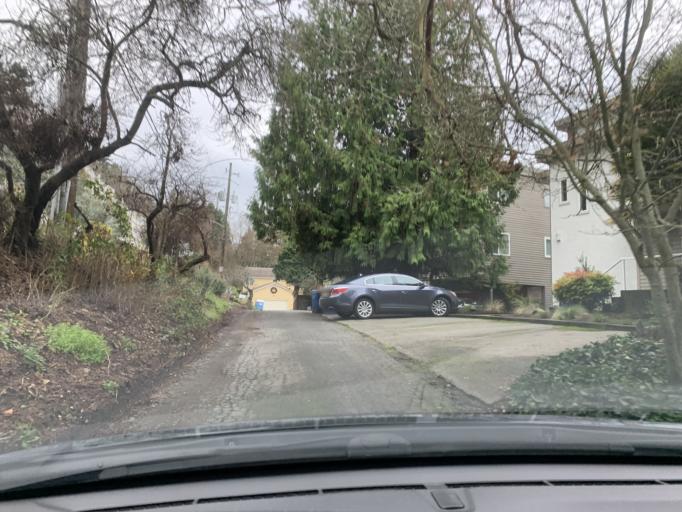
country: US
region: Washington
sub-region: King County
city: White Center
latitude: 47.5657
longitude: -122.4072
